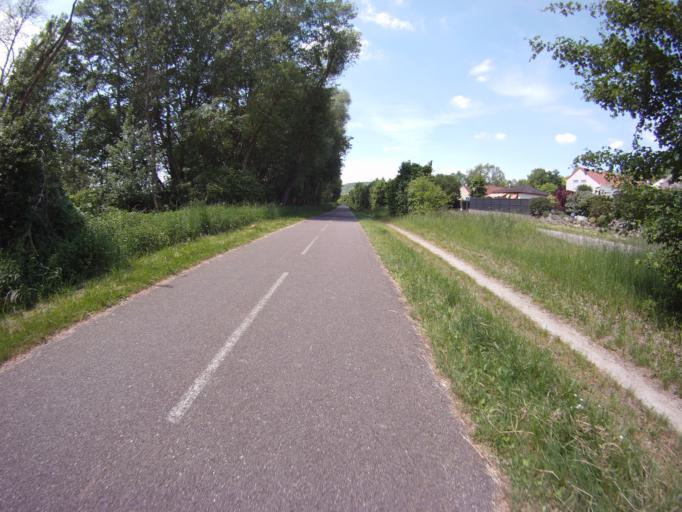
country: FR
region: Lorraine
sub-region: Departement de Meurthe-et-Moselle
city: Lay-Saint-Christophe
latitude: 48.7448
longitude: 6.2100
